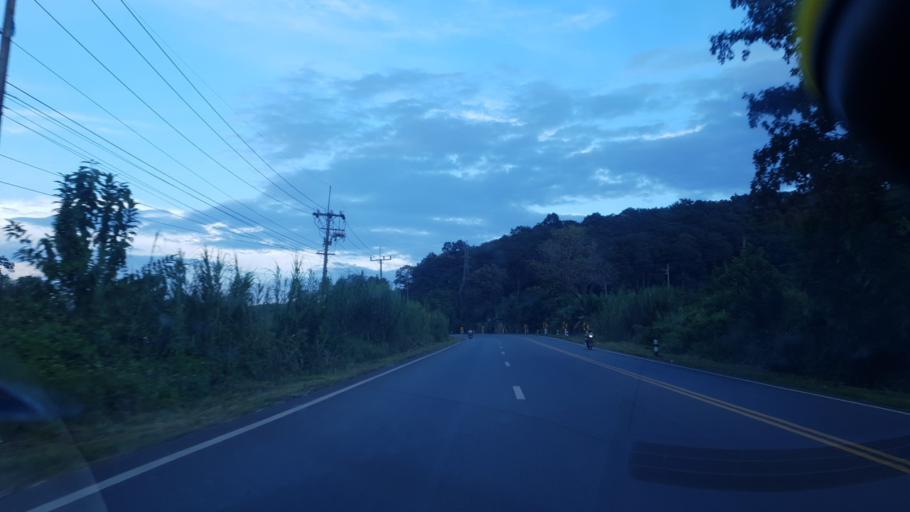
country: TH
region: Chiang Rai
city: Mae Lao
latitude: 19.7325
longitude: 99.6258
